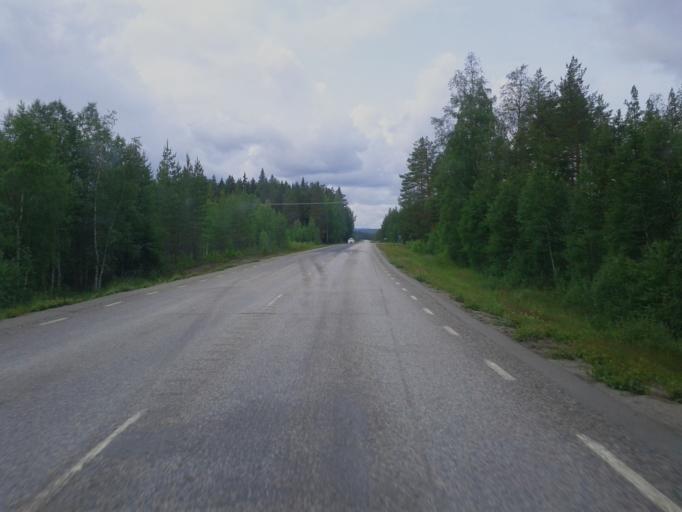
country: SE
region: Vaesterbotten
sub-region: Norsjo Kommun
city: Norsjoe
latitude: 64.9803
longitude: 19.5728
